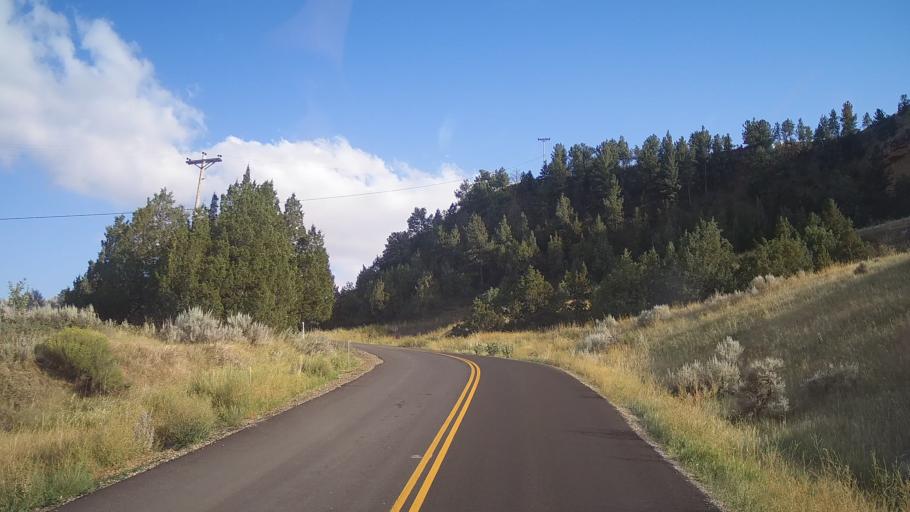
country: US
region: Montana
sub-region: Dawson County
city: Glendive
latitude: 47.0629
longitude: -104.6812
